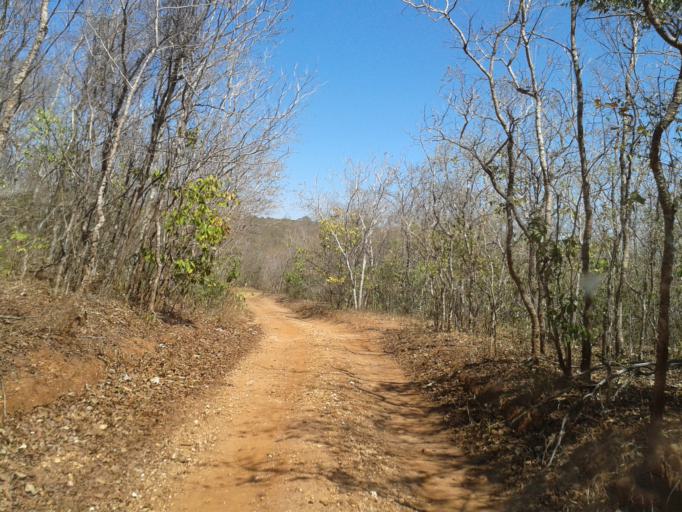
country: BR
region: Minas Gerais
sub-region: Ituiutaba
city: Ituiutaba
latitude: -19.1198
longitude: -49.2972
